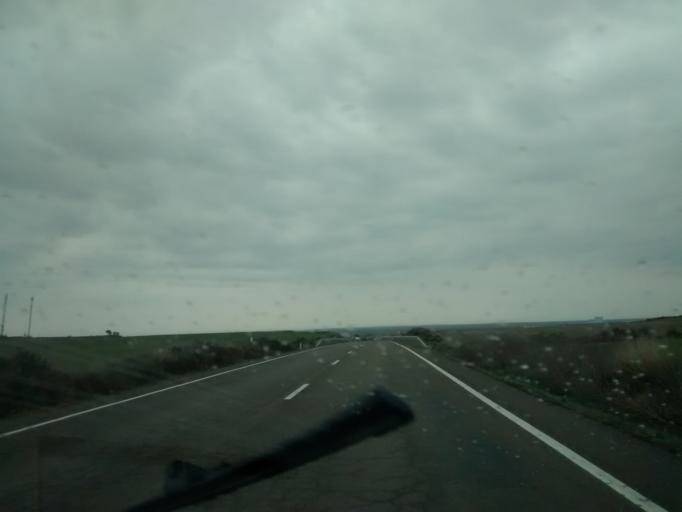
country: ES
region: Aragon
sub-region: Provincia de Zaragoza
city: Bujaraloz
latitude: 41.5097
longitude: -0.1663
